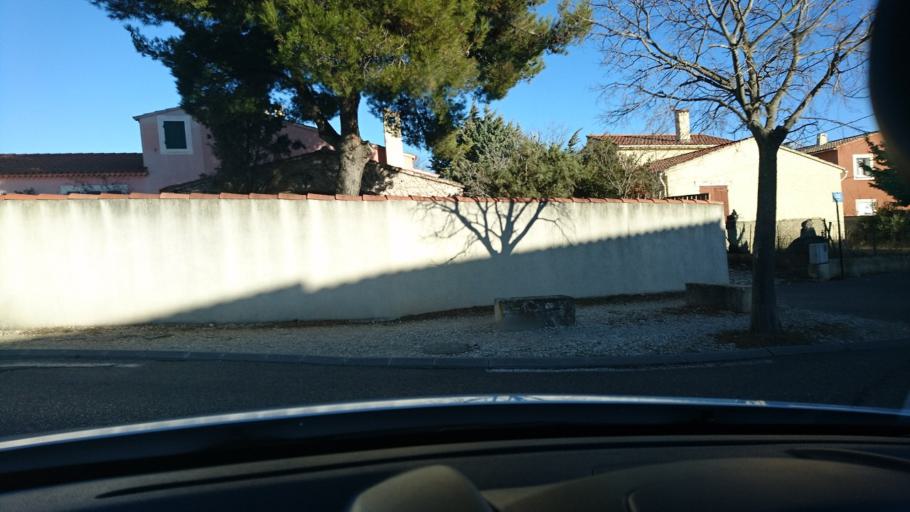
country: FR
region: Languedoc-Roussillon
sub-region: Departement du Gard
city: Les Angles
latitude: 43.9610
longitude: 4.7607
